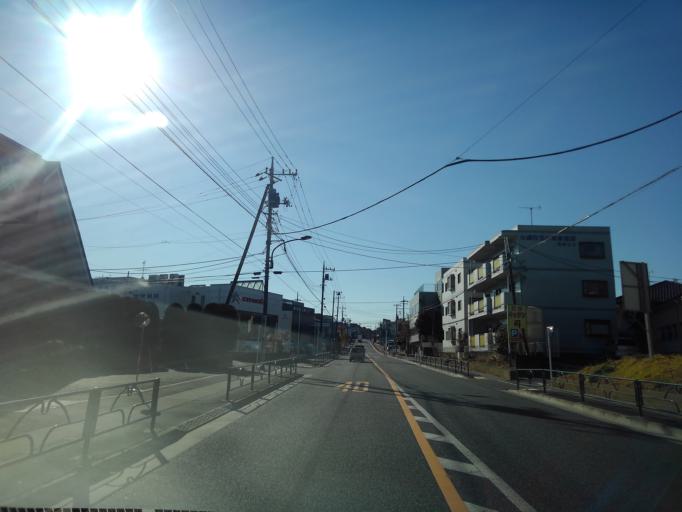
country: JP
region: Tokyo
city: Hino
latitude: 35.6888
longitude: 139.3706
